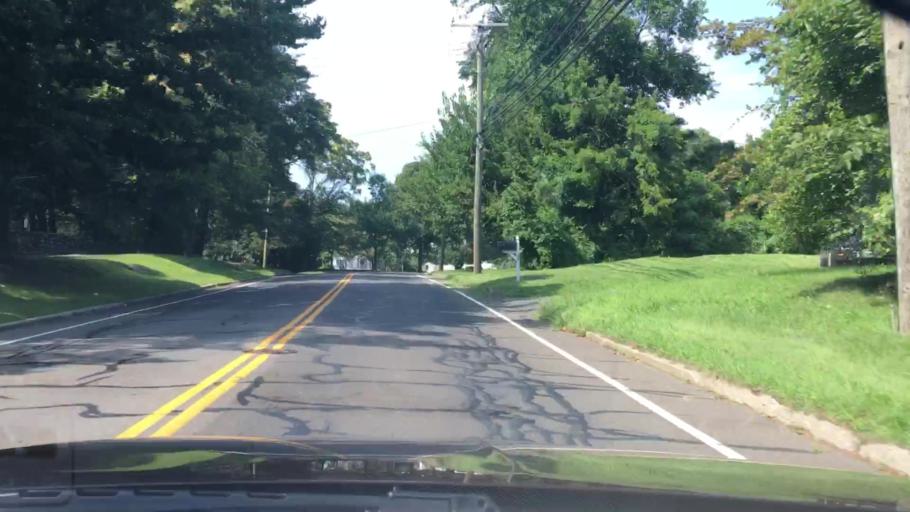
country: US
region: Connecticut
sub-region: Fairfield County
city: Norwalk
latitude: 41.1313
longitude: -73.4135
